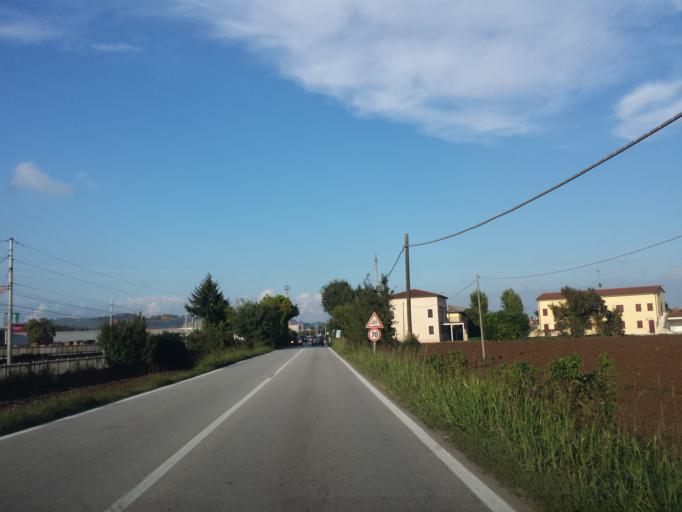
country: IT
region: Veneto
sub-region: Provincia di Vicenza
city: Tavernelle
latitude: 45.5072
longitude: 11.4506
